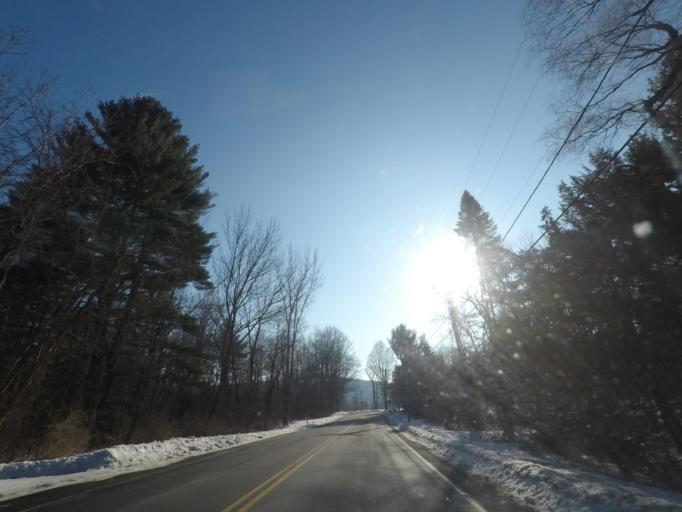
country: US
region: Massachusetts
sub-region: Berkshire County
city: Richmond
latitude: 42.5003
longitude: -73.4367
